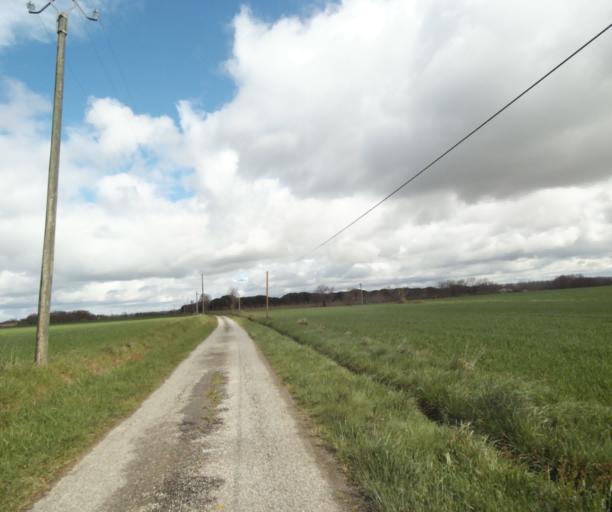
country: FR
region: Midi-Pyrenees
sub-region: Departement de l'Ariege
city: Saverdun
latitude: 43.2343
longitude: 1.5488
